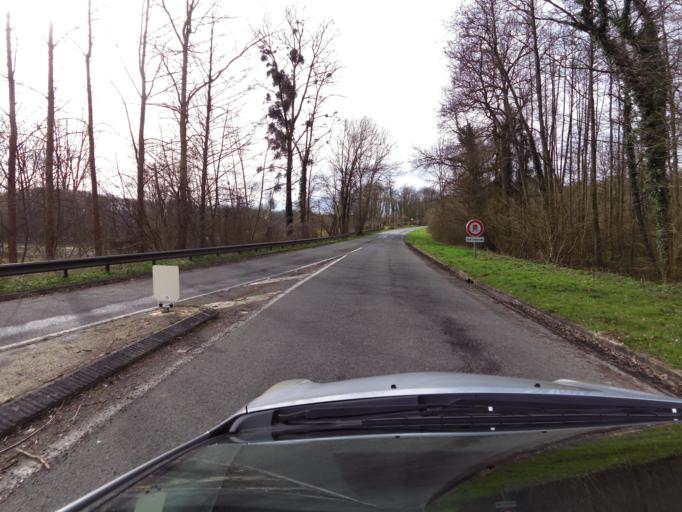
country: FR
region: Picardie
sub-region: Departement de l'Oise
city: Ver-sur-Launette
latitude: 49.1154
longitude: 2.6859
